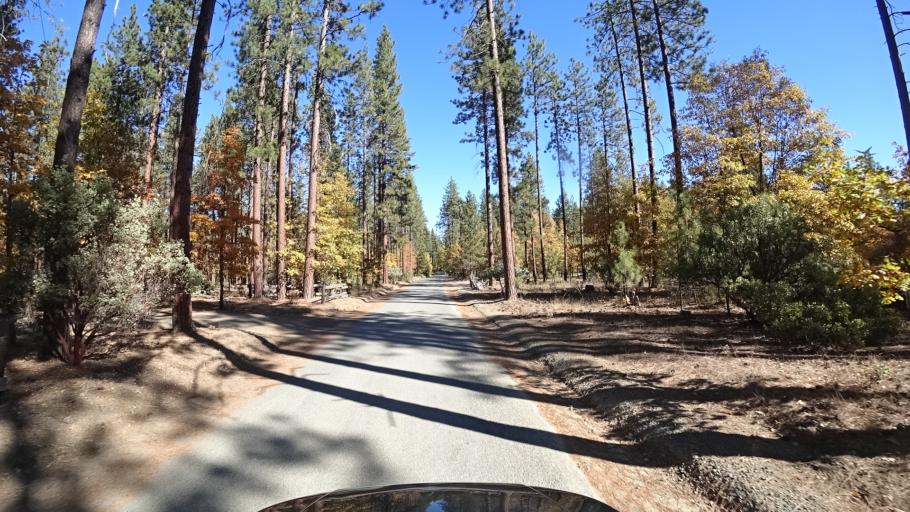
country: US
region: California
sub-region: Siskiyou County
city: Yreka
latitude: 41.5160
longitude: -122.9036
